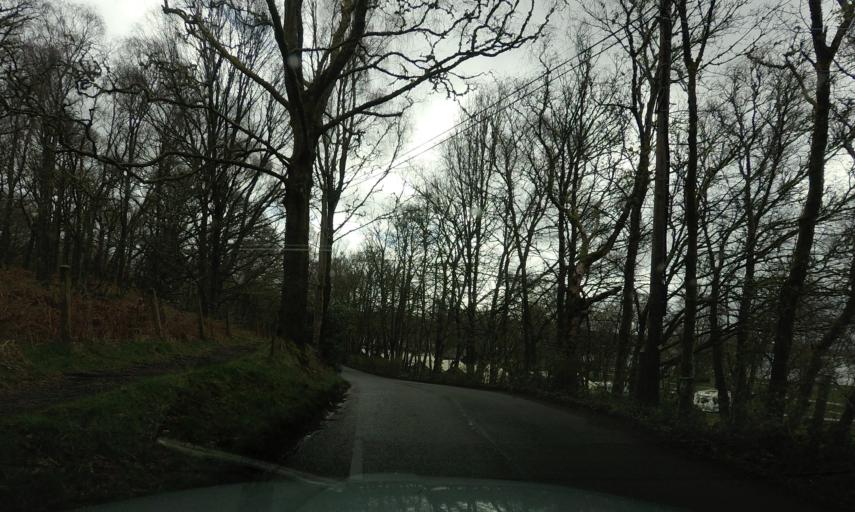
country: GB
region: Scotland
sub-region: West Dunbartonshire
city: Balloch
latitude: 56.1015
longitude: -4.5633
